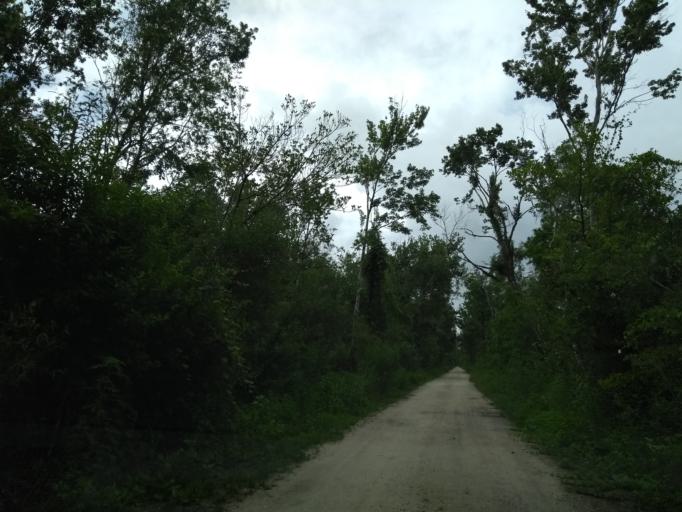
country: US
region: Florida
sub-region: Collier County
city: Lely Resort
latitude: 25.9926
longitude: -81.4111
